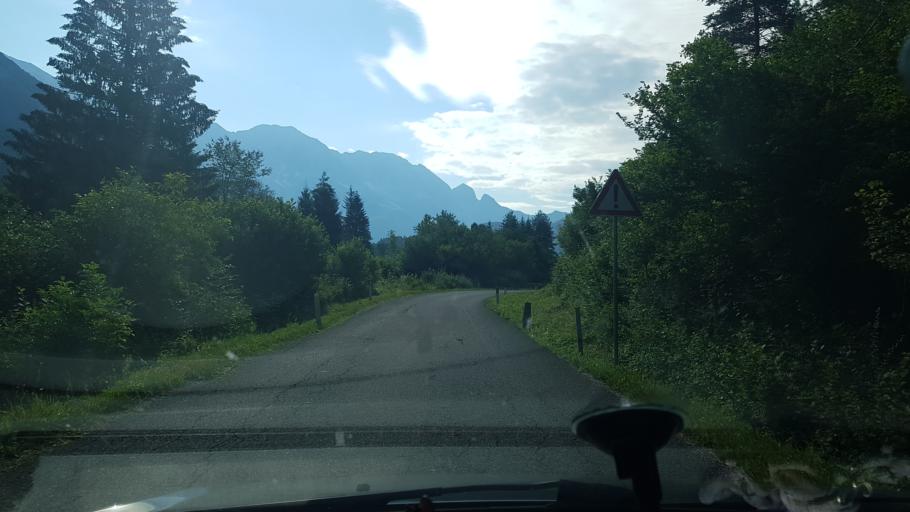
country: IT
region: Friuli Venezia Giulia
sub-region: Provincia di Udine
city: Prato
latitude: 46.3668
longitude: 13.3199
